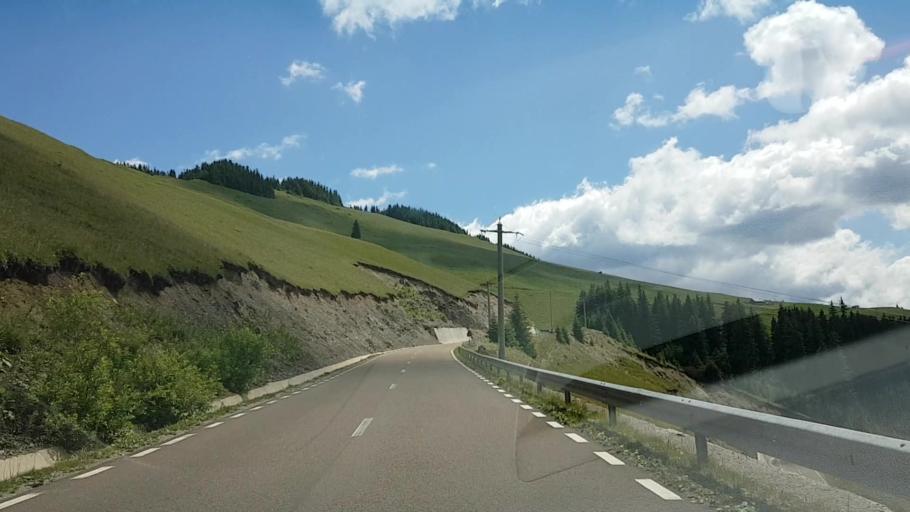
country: RO
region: Suceava
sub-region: Comuna Sadova
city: Sadova
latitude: 47.4594
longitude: 25.5269
